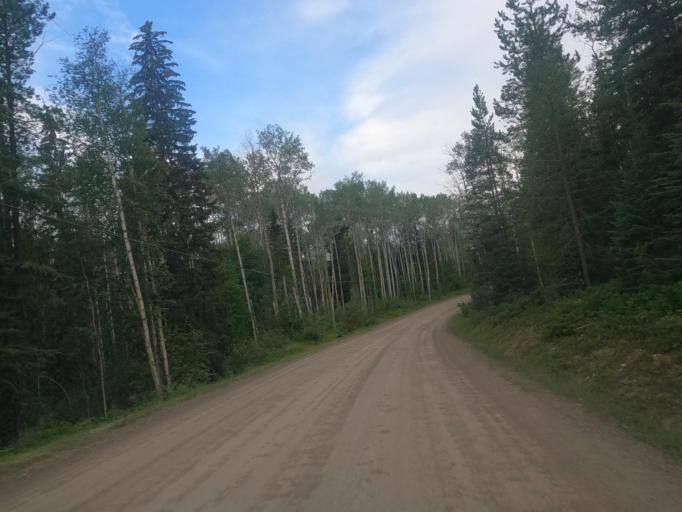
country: CA
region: British Columbia
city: Golden
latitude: 51.4444
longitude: -117.0297
